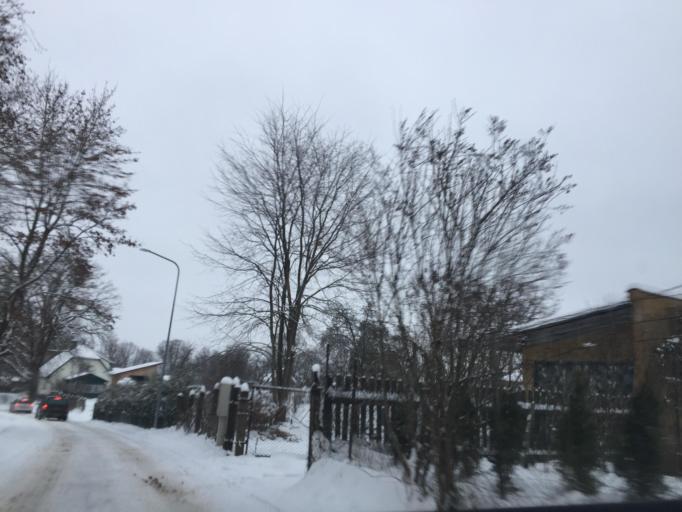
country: LV
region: Smiltene
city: Smiltene
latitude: 57.4204
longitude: 25.8985
